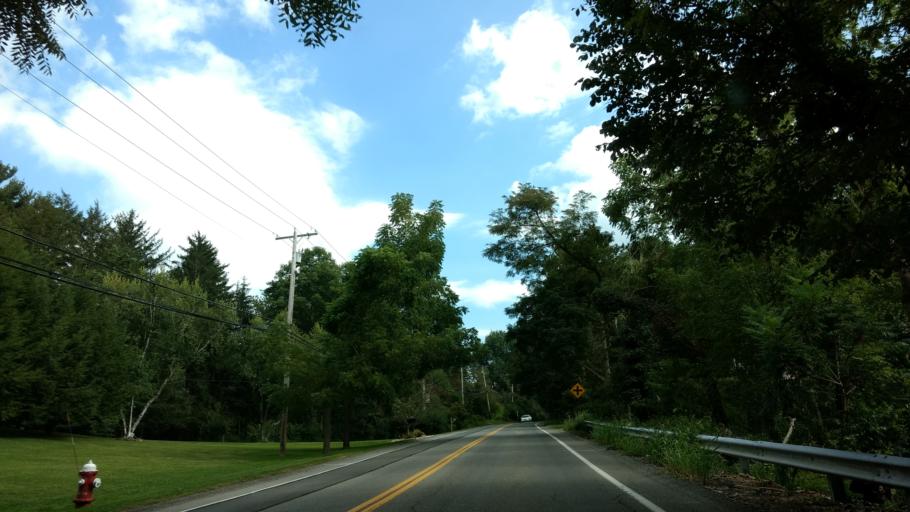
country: US
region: Pennsylvania
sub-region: Allegheny County
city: Franklin Park
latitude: 40.5898
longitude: -80.0722
